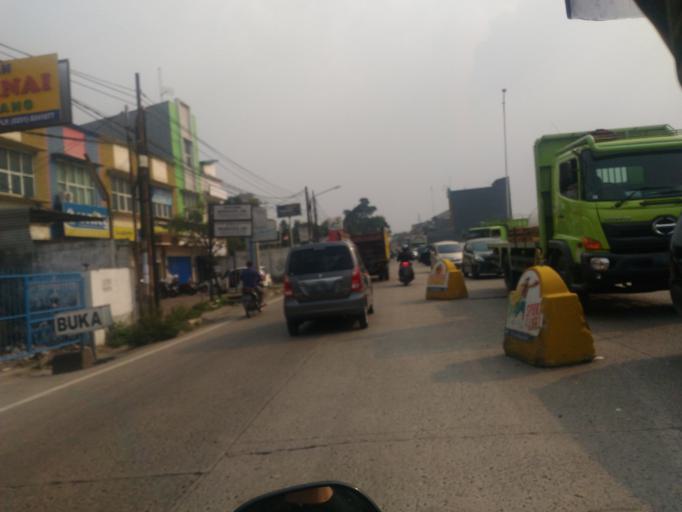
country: ID
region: West Java
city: Caringin
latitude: -6.6590
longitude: 106.8457
